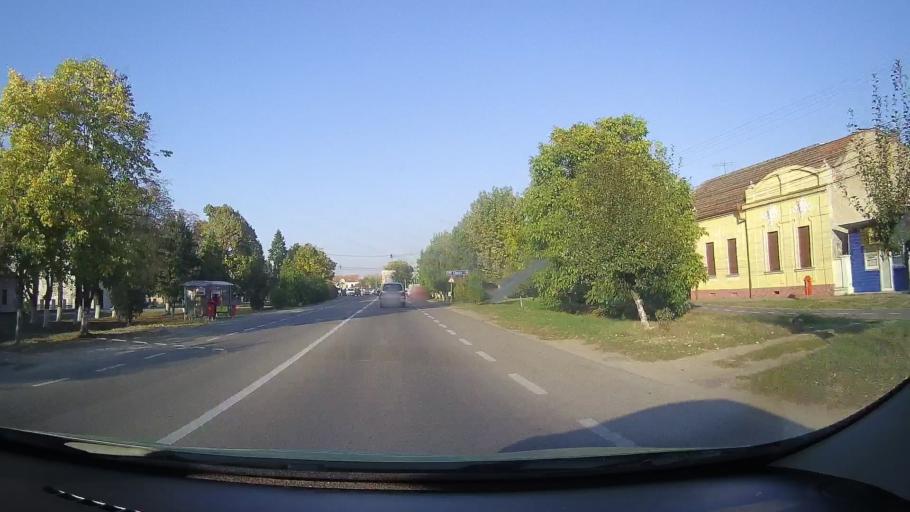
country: RO
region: Arad
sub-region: Comuna Pancota
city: Pancota
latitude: 46.3229
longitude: 21.6876
